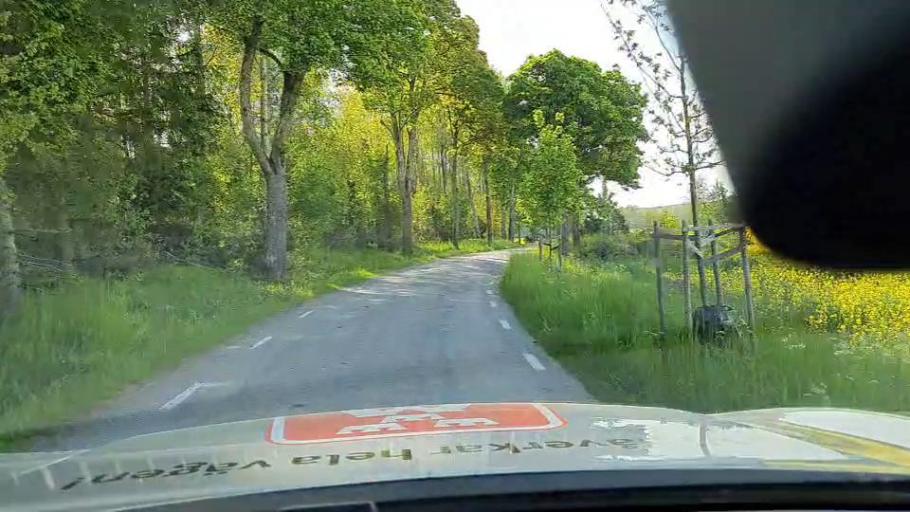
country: SE
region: Soedermanland
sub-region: Eskilstuna Kommun
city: Arla
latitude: 59.2586
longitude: 16.6732
